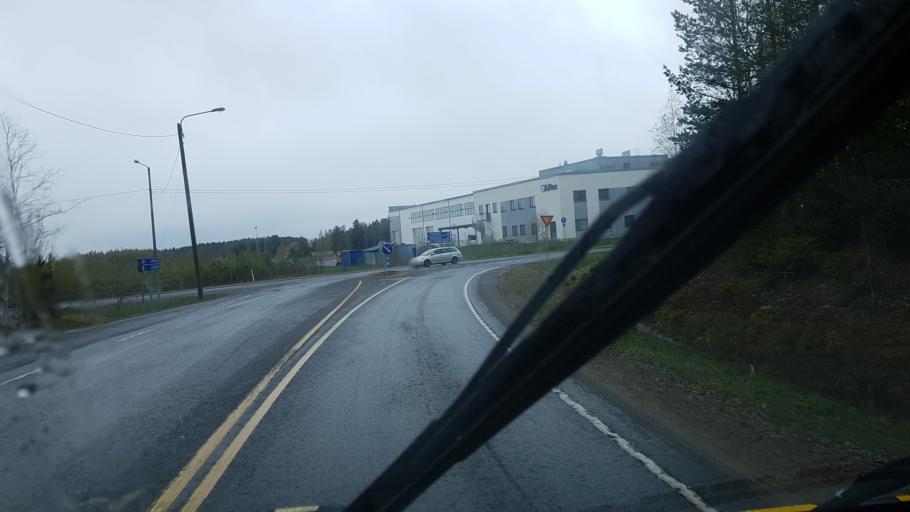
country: FI
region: Pirkanmaa
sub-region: Tampere
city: Pirkkala
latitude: 61.4299
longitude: 23.6219
